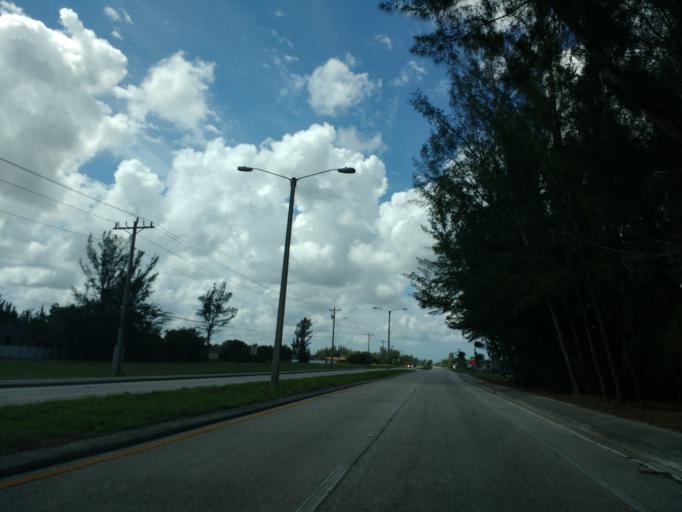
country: US
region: Florida
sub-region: Lee County
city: Cape Coral
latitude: 26.6310
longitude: -82.0071
